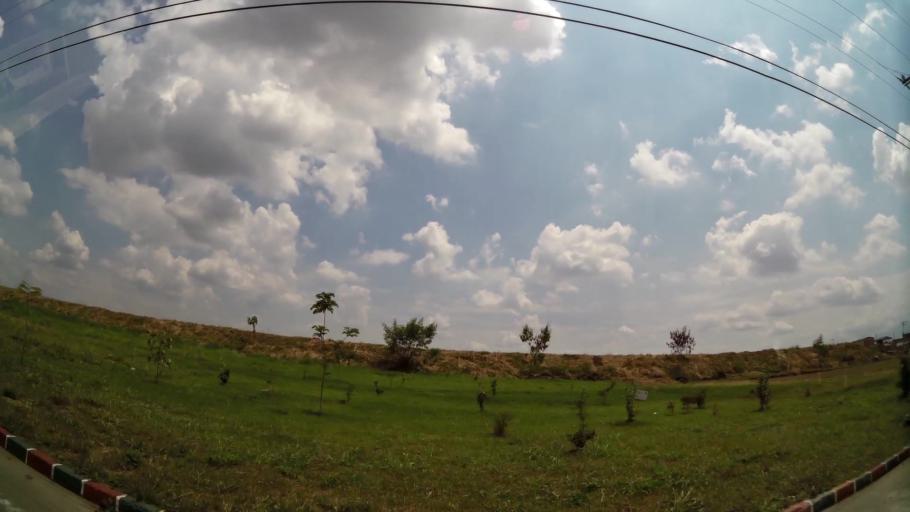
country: CO
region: Valle del Cauca
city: Cali
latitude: 3.4587
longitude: -76.4612
